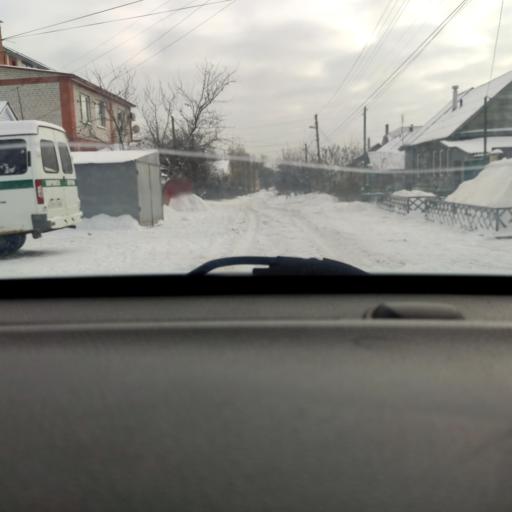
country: RU
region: Voronezj
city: Somovo
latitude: 51.7360
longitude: 39.2766
